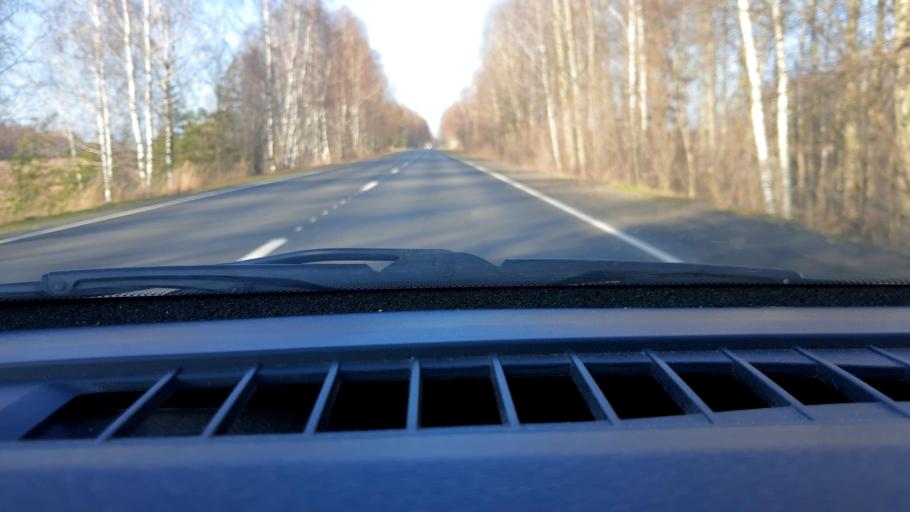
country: RU
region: Nizjnij Novgorod
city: Novaya Balakhna
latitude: 56.5560
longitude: 43.7389
